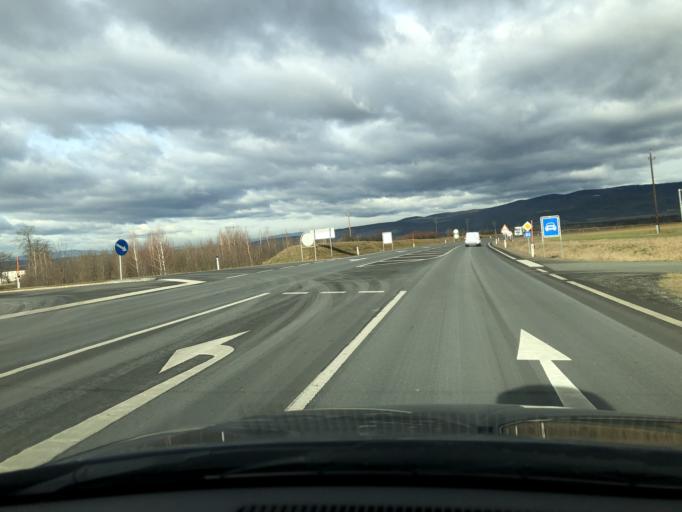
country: AT
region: Burgenland
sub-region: Politischer Bezirk Oberwart
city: Schachendorf
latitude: 47.2623
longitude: 16.4503
